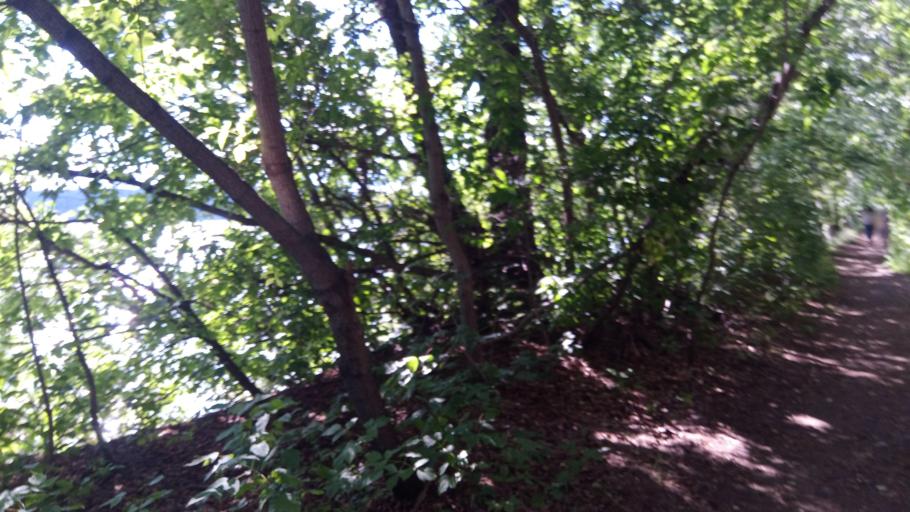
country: RU
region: Chelyabinsk
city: Chebarkul'
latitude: 55.0161
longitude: 60.3130
